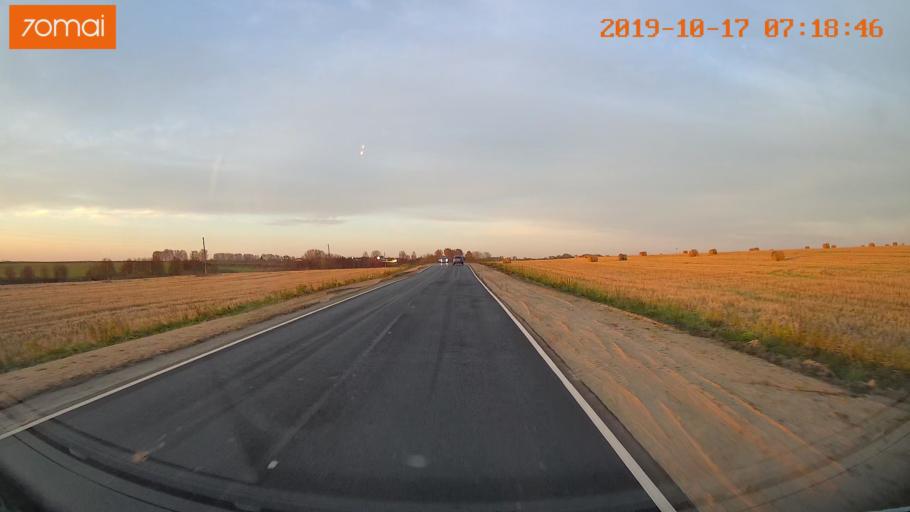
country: RU
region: Ivanovo
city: Gavrilov Posad
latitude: 56.3503
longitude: 40.2125
